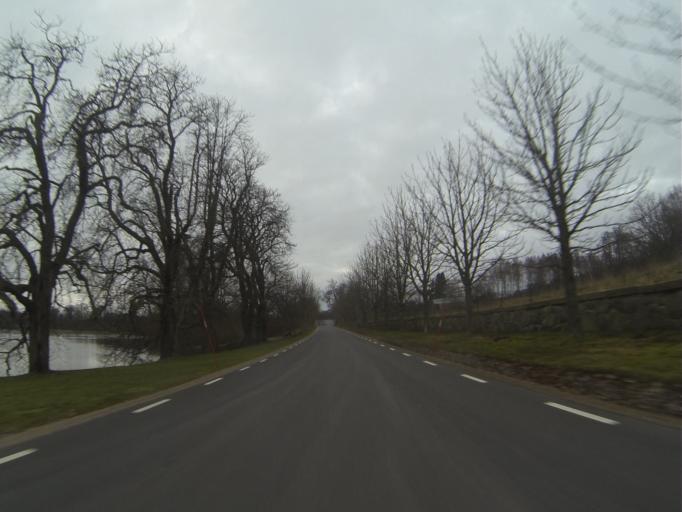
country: SE
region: Skane
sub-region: Lunds Kommun
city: Genarp
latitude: 55.5808
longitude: 13.4310
